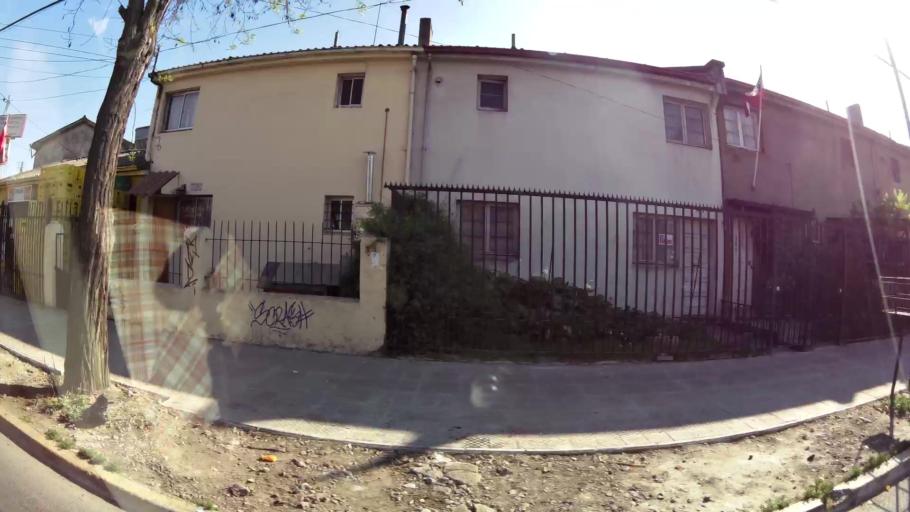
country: CL
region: Santiago Metropolitan
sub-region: Provincia de Santiago
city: Santiago
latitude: -33.4089
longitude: -70.6665
